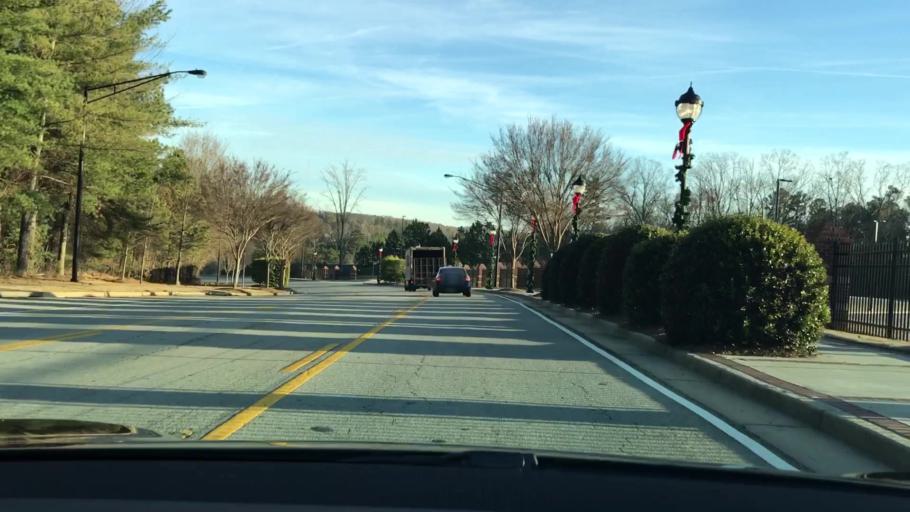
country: US
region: Georgia
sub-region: Gwinnett County
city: Buford
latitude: 34.1289
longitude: -83.9858
